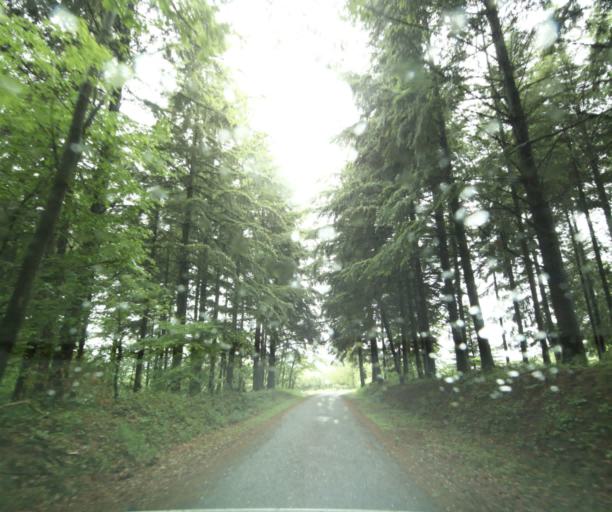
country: FR
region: Bourgogne
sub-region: Departement de Saone-et-Loire
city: Charolles
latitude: 46.4786
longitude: 4.4137
